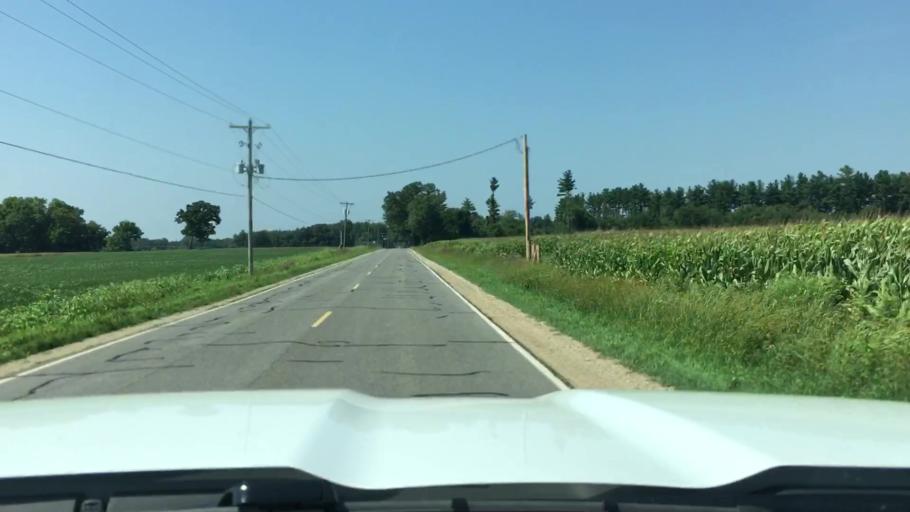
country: US
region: Michigan
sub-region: Saint Joseph County
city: Three Rivers
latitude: 41.9985
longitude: -85.5926
